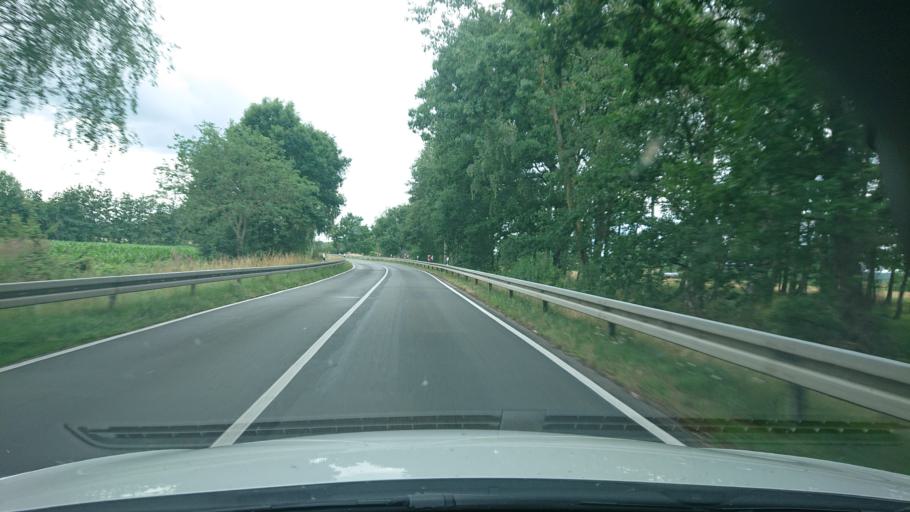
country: DE
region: Mecklenburg-Vorpommern
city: Ludwigslust
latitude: 53.3515
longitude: 11.4302
